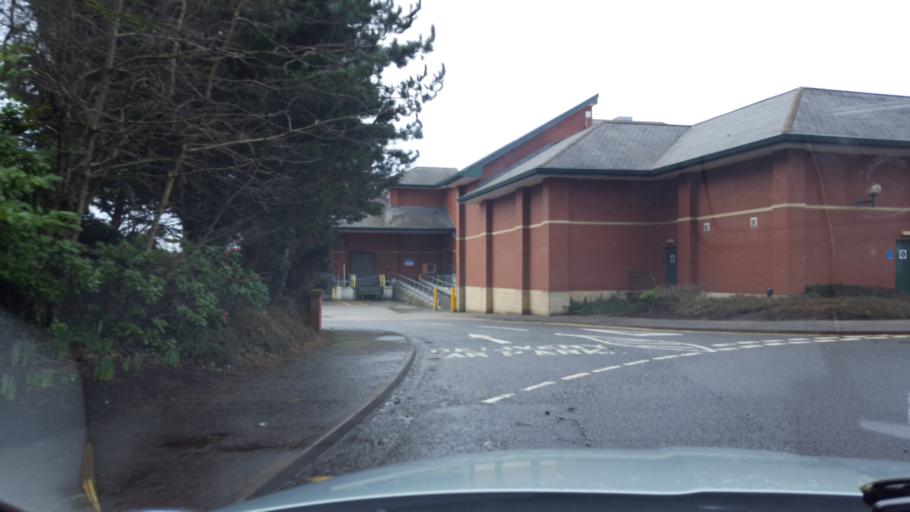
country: GB
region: Scotland
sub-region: South Ayrshire
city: Ayr
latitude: 55.4553
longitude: -4.6250
